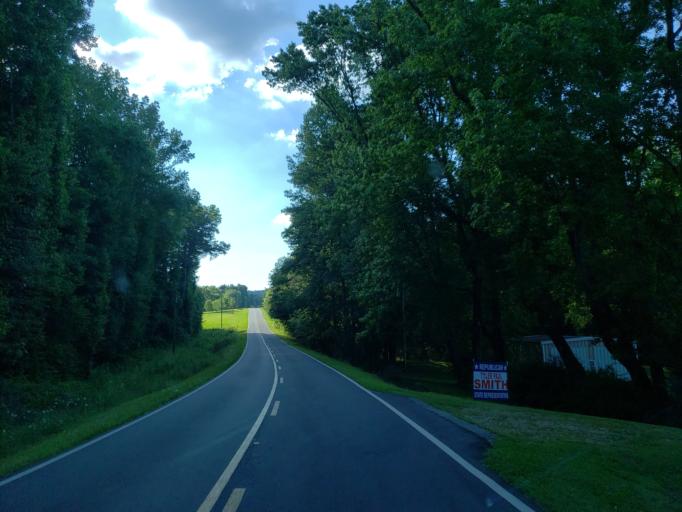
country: US
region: Georgia
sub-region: Haralson County
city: Bremen
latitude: 33.6782
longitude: -85.1251
